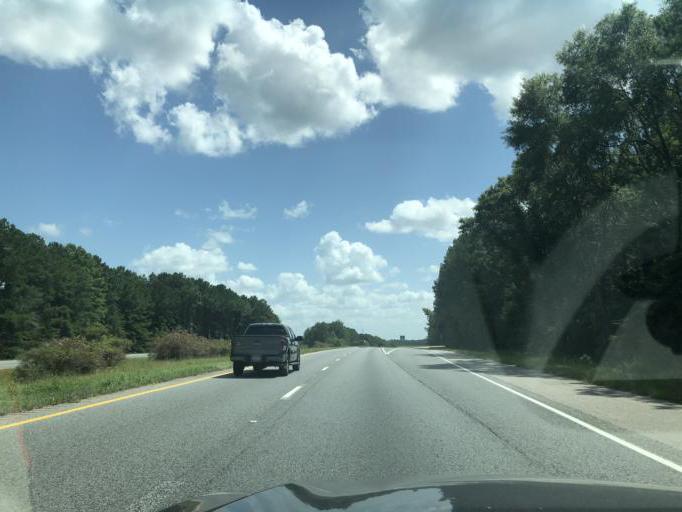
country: US
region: Georgia
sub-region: Troup County
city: La Grange
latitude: 33.0186
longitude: -84.9520
